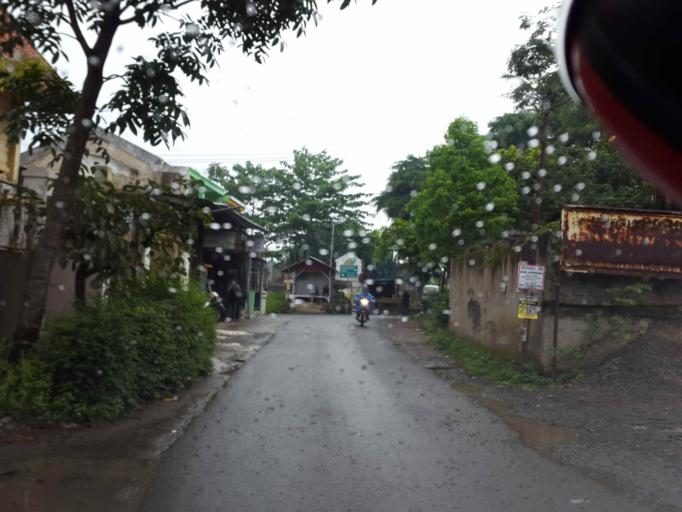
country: ID
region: West Java
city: Cimahi
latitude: -6.8686
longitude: 107.5703
